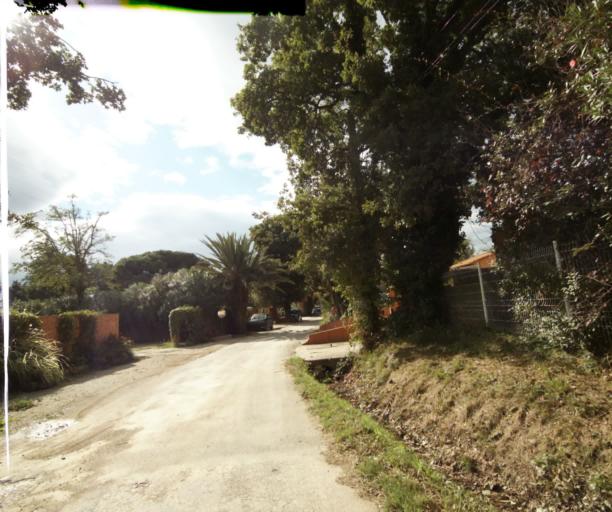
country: FR
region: Languedoc-Roussillon
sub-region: Departement des Pyrenees-Orientales
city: Argelers
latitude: 42.5728
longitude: 3.0263
